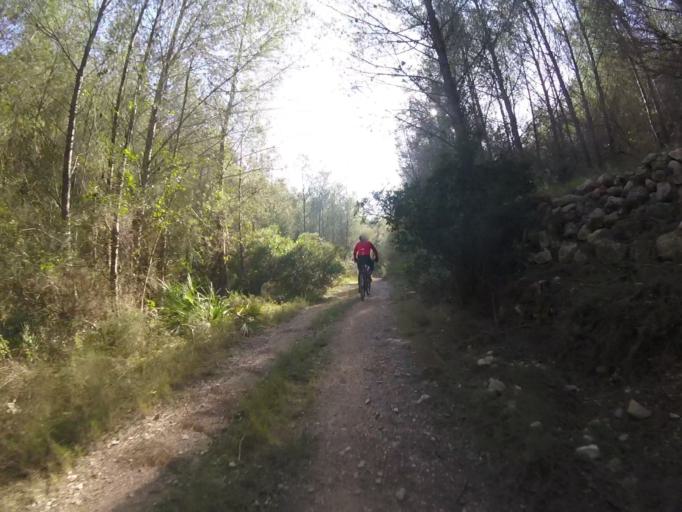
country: ES
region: Valencia
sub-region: Provincia de Castello
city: Santa Magdalena de Pulpis
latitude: 40.3094
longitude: 0.3338
